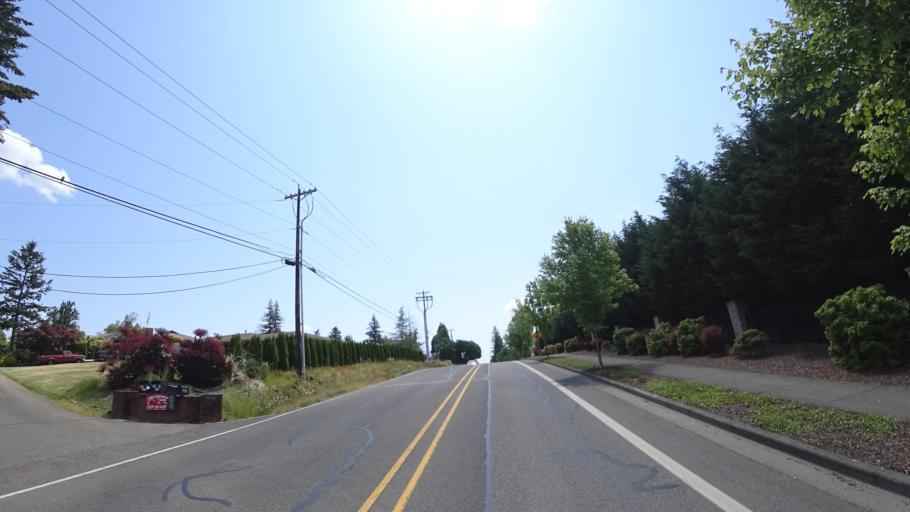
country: US
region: Oregon
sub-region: Clackamas County
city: Happy Valley
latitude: 45.4549
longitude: -122.5400
